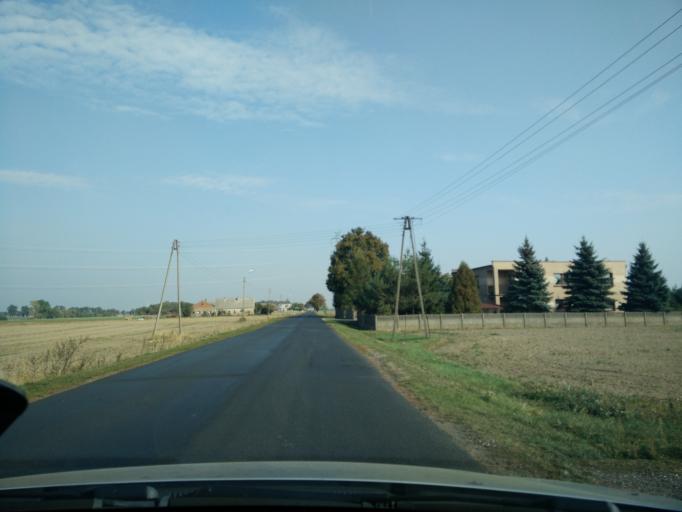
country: PL
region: Greater Poland Voivodeship
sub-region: Powiat sredzki
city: Dominowo
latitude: 52.2957
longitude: 17.3390
